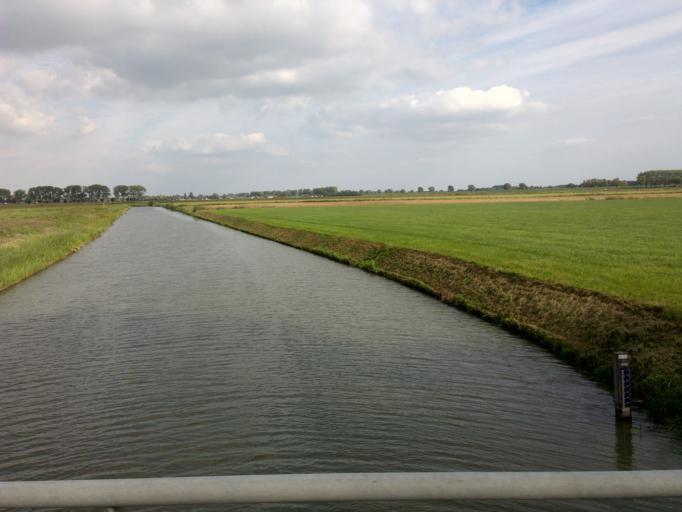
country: NL
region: North Brabant
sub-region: Gemeente Waalwijk
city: Waalwijk
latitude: 51.7251
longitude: 5.0565
